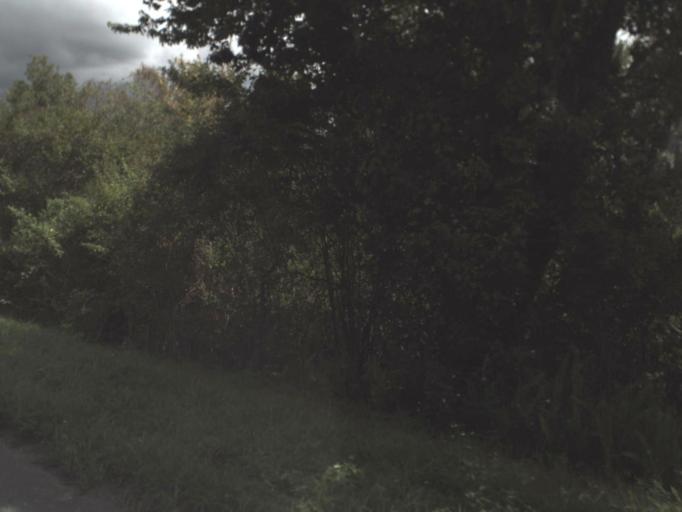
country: US
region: Florida
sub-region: Hillsborough County
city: Balm
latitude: 27.6431
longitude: -82.0584
